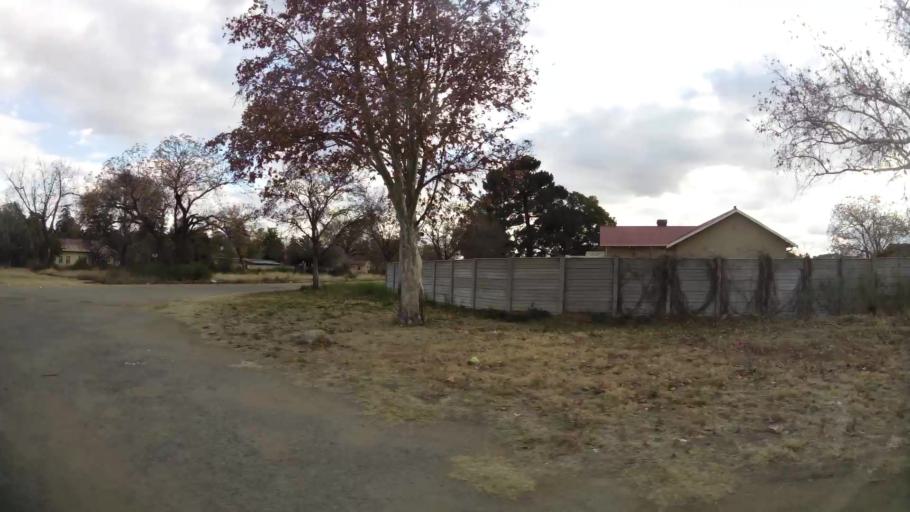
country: ZA
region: Orange Free State
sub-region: Lejweleputswa District Municipality
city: Welkom
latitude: -27.9907
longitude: 26.7099
